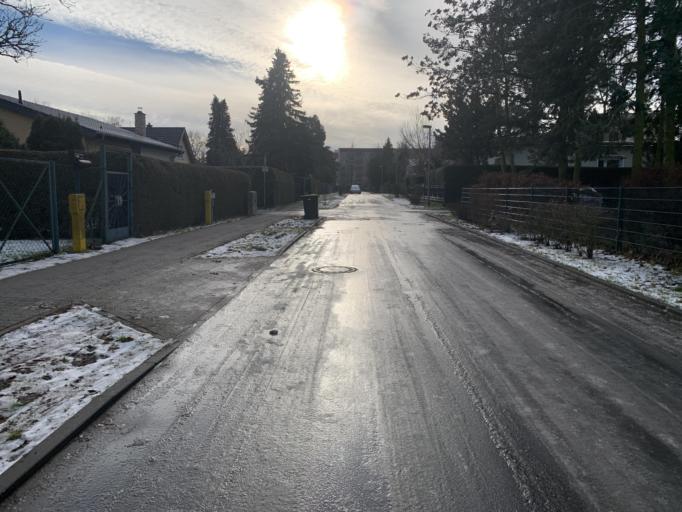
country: DE
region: Brandenburg
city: Oranienburg
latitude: 52.7451
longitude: 13.2466
